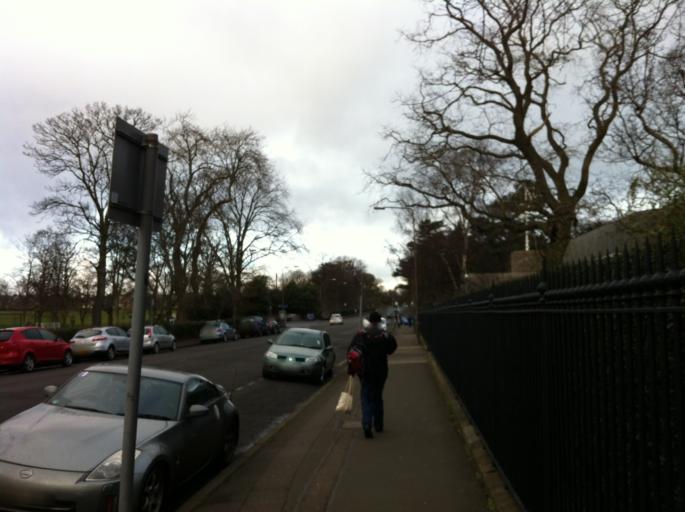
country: GB
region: Scotland
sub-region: Edinburgh
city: Edinburgh
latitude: 55.9635
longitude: -3.2122
